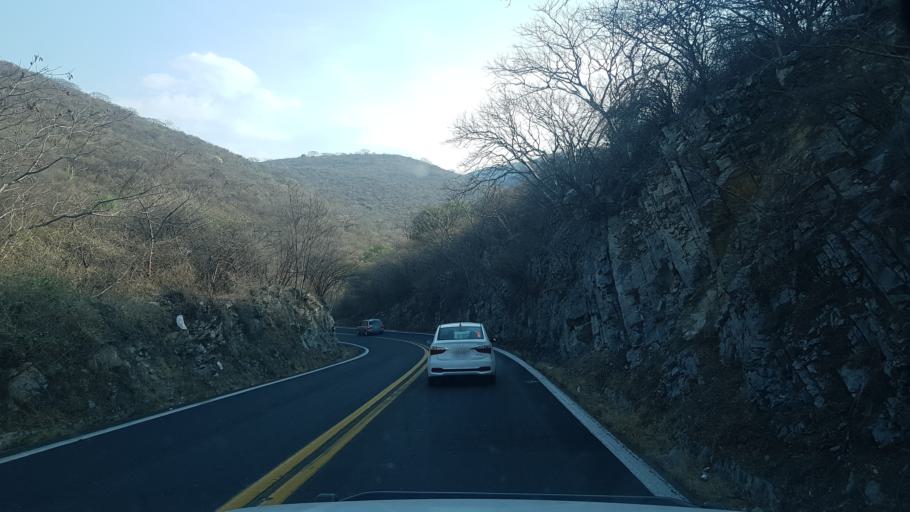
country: MX
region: Puebla
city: Calmeca
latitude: 18.6537
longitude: -98.6508
